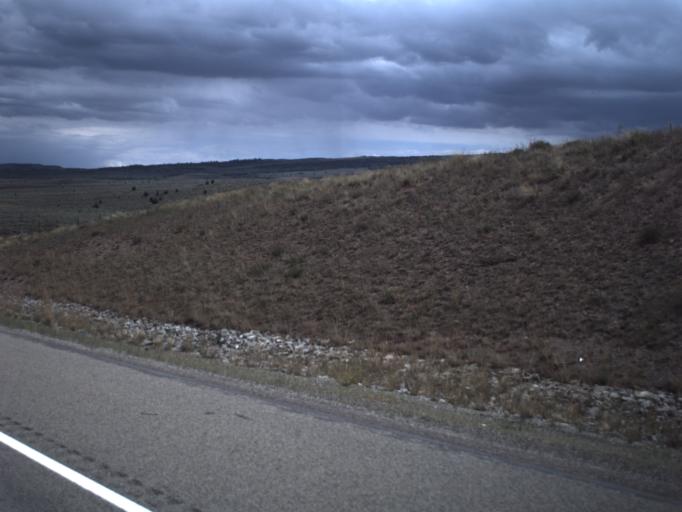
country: US
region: Utah
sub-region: Carbon County
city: Helper
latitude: 39.8447
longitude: -111.0000
